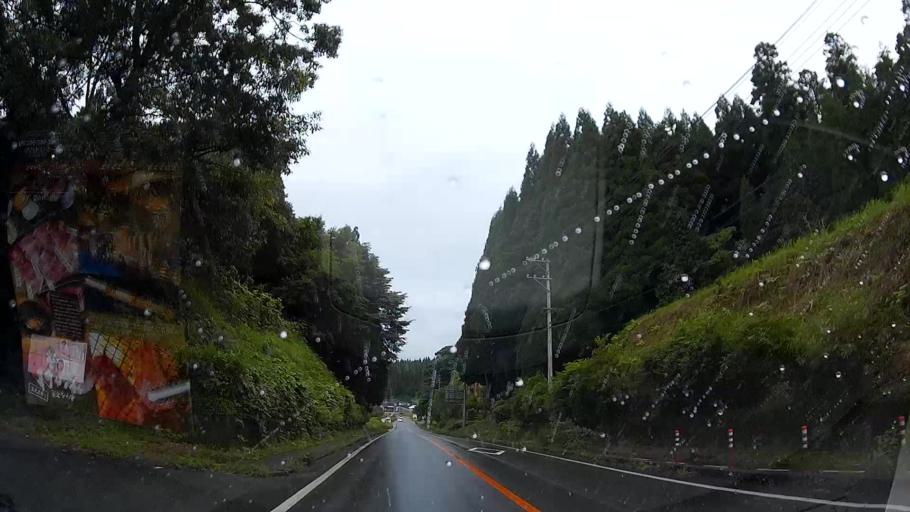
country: JP
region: Oita
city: Tsukawaki
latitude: 33.1310
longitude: 131.0633
